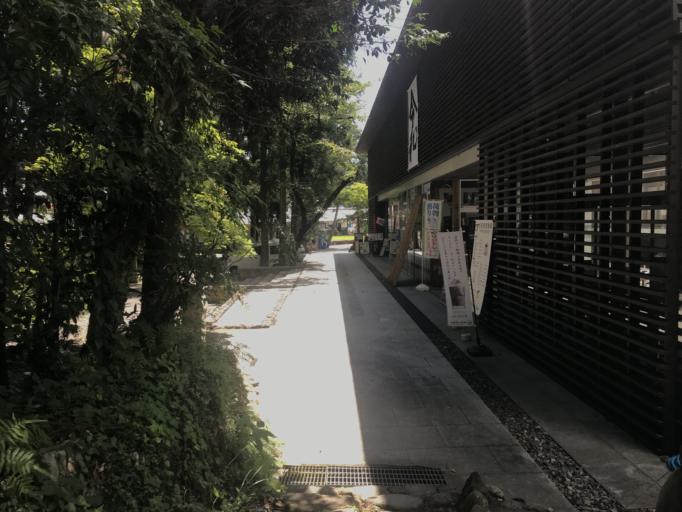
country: JP
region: Wakayama
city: Shingu
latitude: 33.8391
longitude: 135.7743
